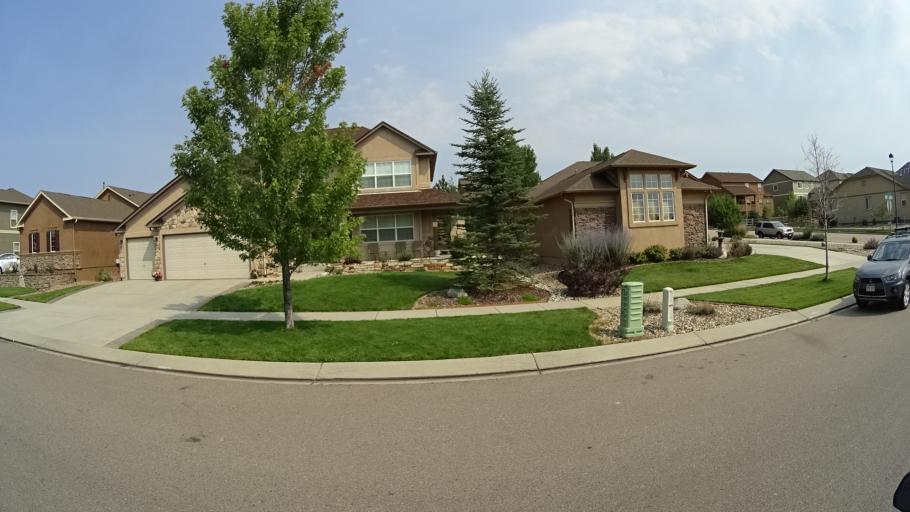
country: US
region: Colorado
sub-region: El Paso County
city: Black Forest
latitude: 38.9655
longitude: -104.7173
